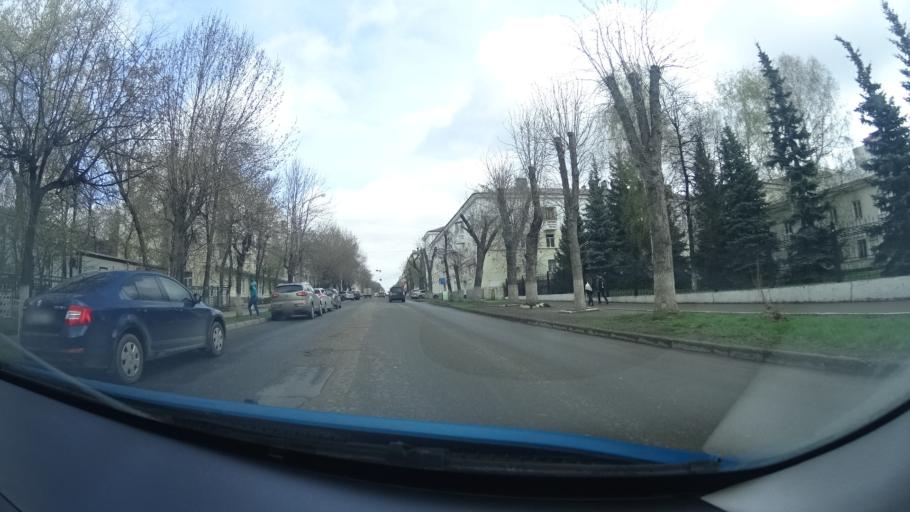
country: RU
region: Bashkortostan
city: Ufa
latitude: 54.7326
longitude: 55.9624
